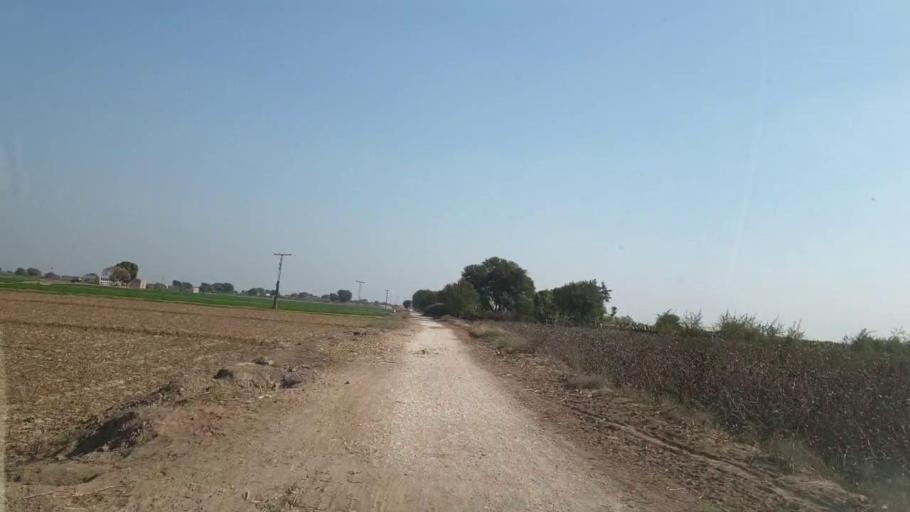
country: PK
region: Sindh
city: Tando Jam
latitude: 25.5083
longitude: 68.4893
